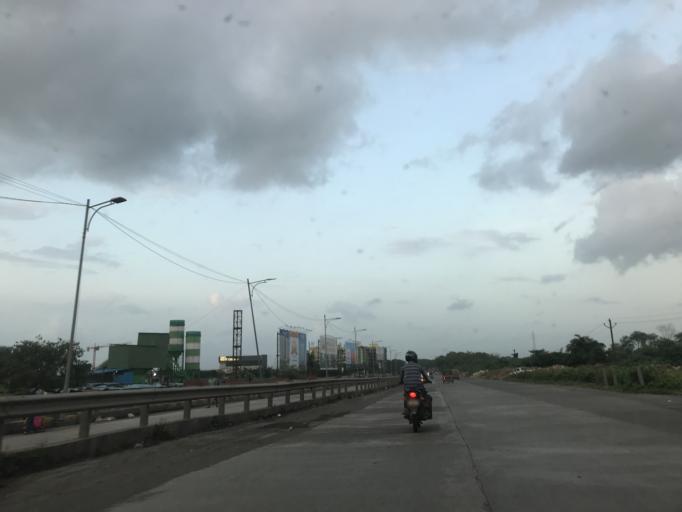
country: IN
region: Maharashtra
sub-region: Thane
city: Thane
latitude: 19.2232
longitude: 72.9923
